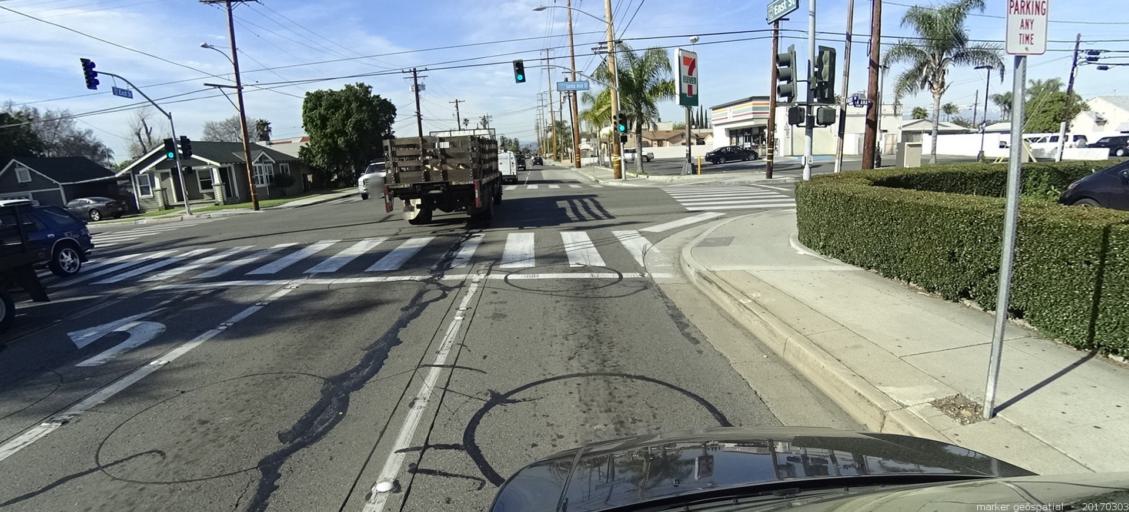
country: US
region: California
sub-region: Orange County
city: Anaheim
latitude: 33.8335
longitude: -117.9011
